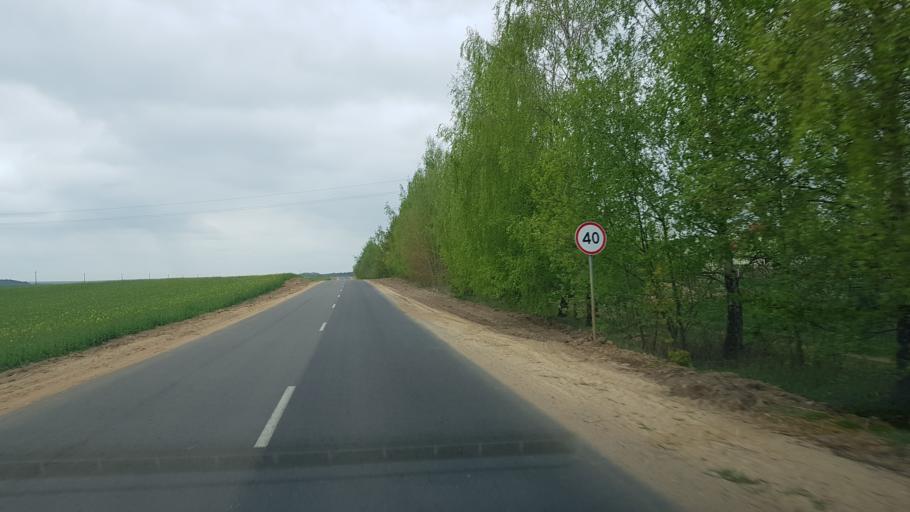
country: BY
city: Fanipol
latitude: 53.7213
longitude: 27.2995
